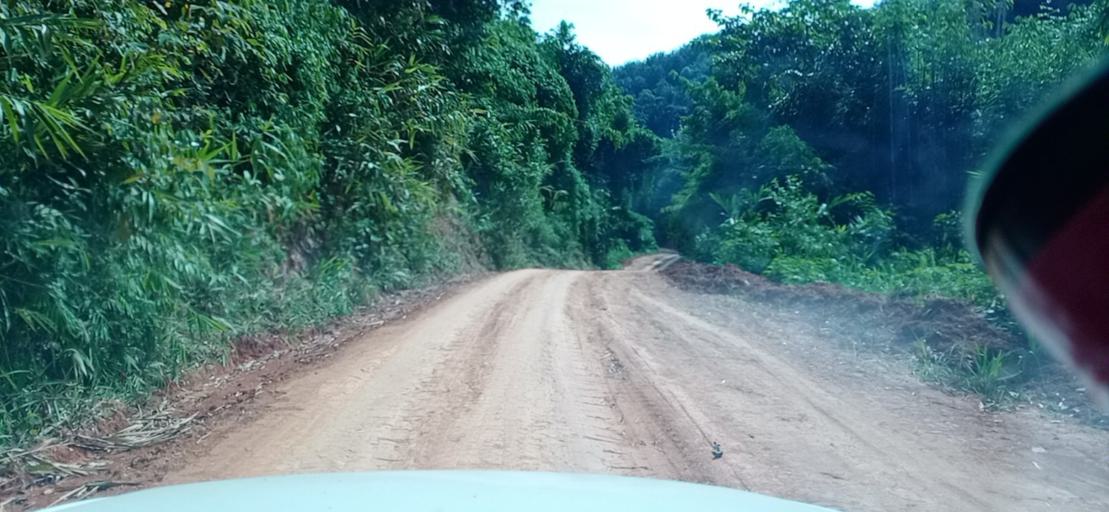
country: TH
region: Changwat Bueng Kan
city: Pak Khat
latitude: 18.6341
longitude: 103.2610
